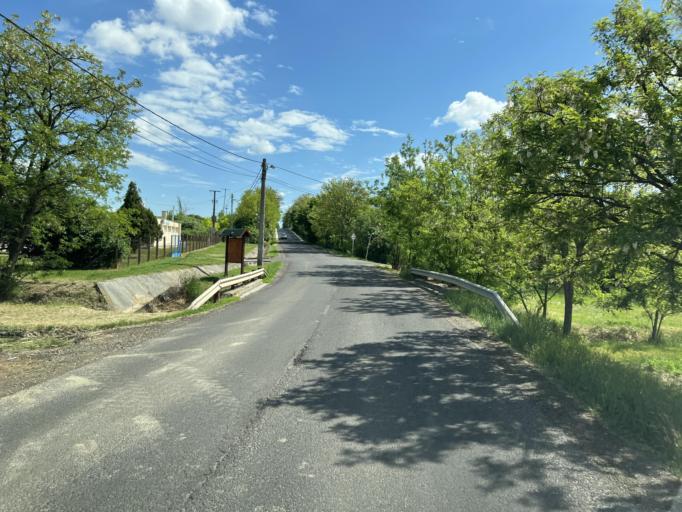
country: HU
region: Pest
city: Valko
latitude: 47.5671
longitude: 19.5214
